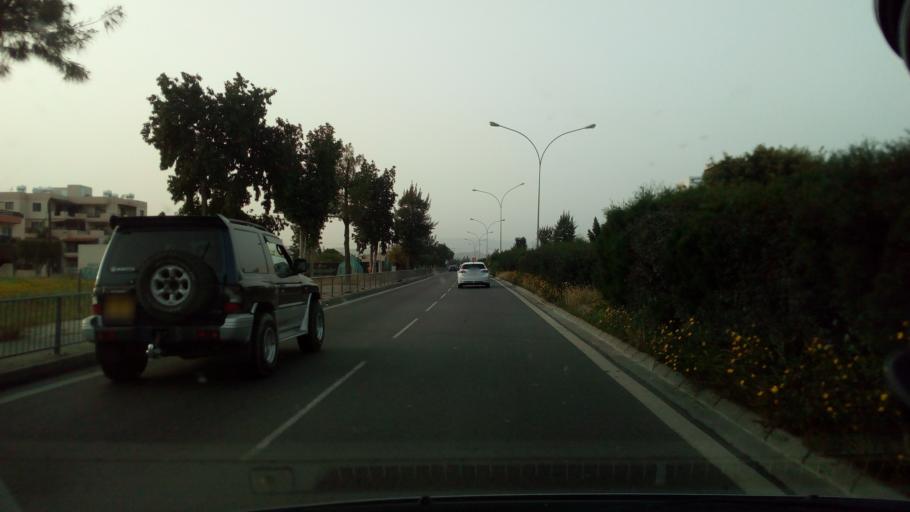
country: CY
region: Limassol
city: Limassol
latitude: 34.6768
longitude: 33.0112
